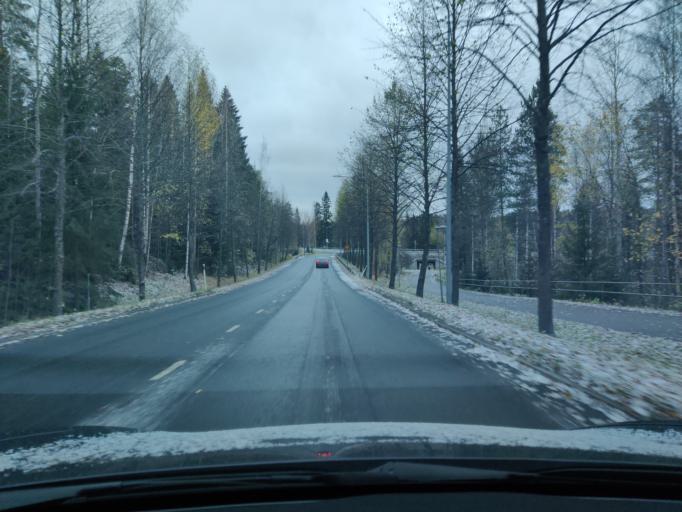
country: FI
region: Northern Savo
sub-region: Kuopio
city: Kuopio
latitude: 62.8406
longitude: 27.6348
